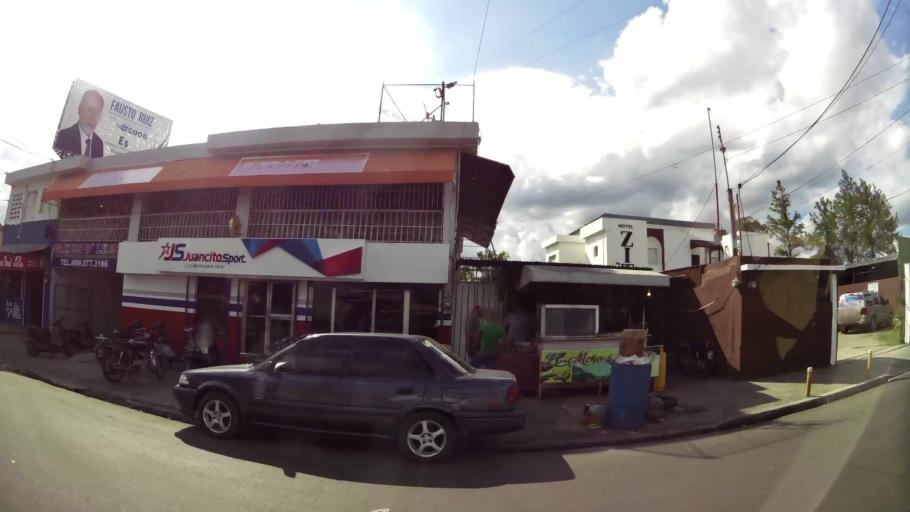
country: DO
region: La Vega
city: Concepcion de La Vega
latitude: 19.2302
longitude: -70.5308
